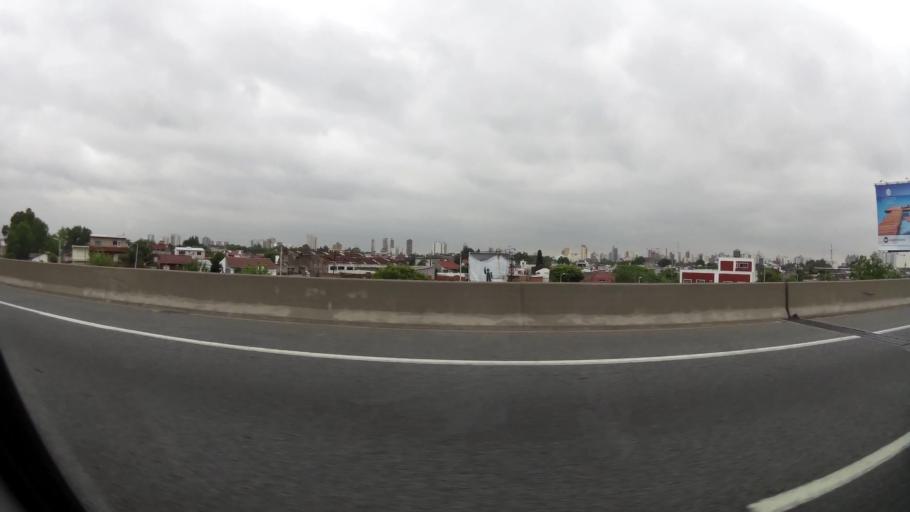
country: AR
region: Buenos Aires
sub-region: Partido de Avellaneda
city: Avellaneda
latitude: -34.6613
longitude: -58.3468
